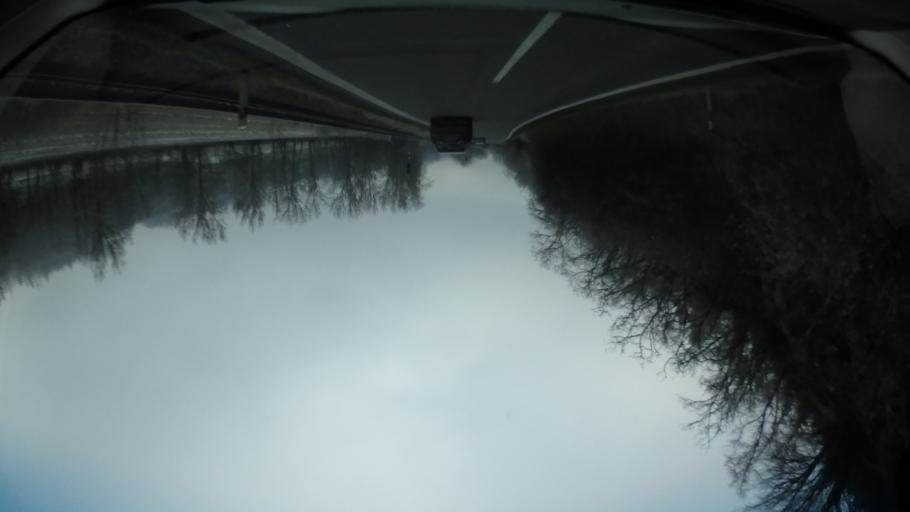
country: CZ
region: Vysocina
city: Vladislav
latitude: 49.2139
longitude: 15.9530
